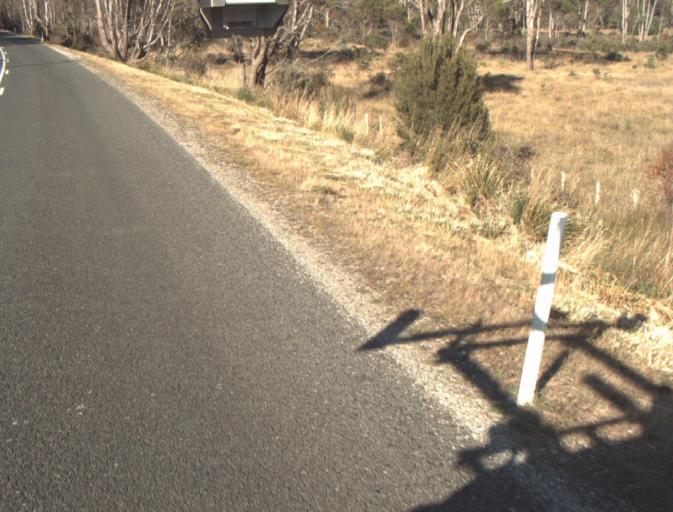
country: AU
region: Tasmania
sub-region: Launceston
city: Mayfield
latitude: -41.3268
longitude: 147.1836
